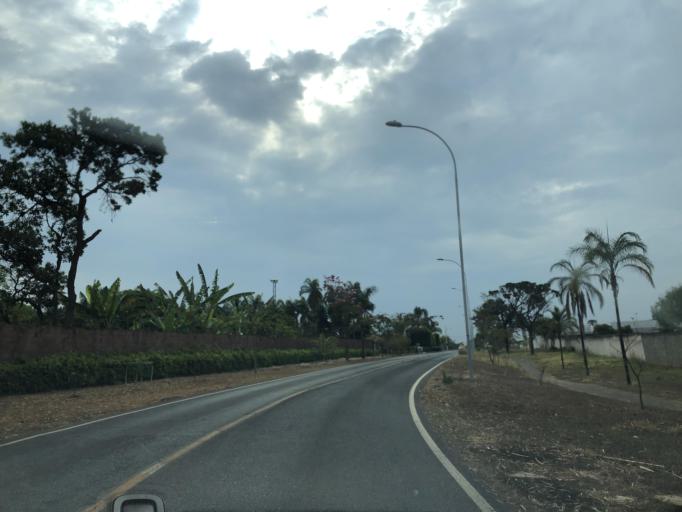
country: BR
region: Federal District
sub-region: Brasilia
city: Brasilia
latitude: -15.9444
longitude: -47.9857
